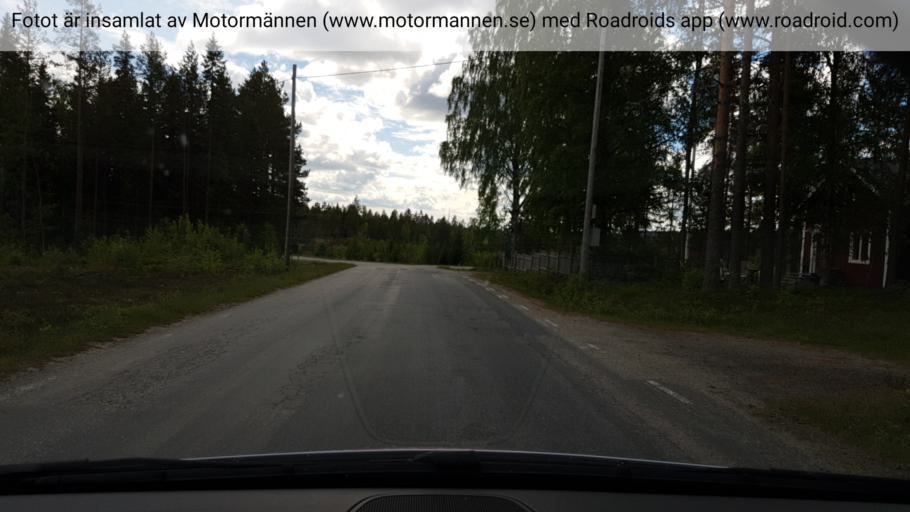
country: SE
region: Vaesterbotten
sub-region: Umea Kommun
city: Roback
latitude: 64.0141
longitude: 20.0810
